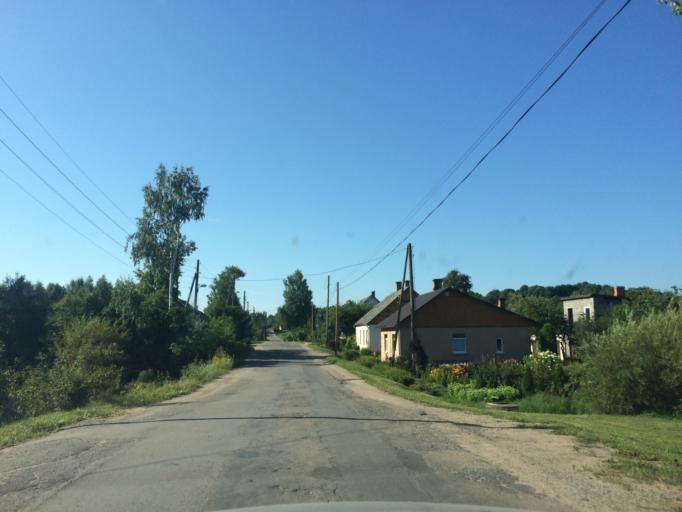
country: LV
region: Rezekne
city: Rezekne
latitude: 56.4904
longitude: 27.3350
